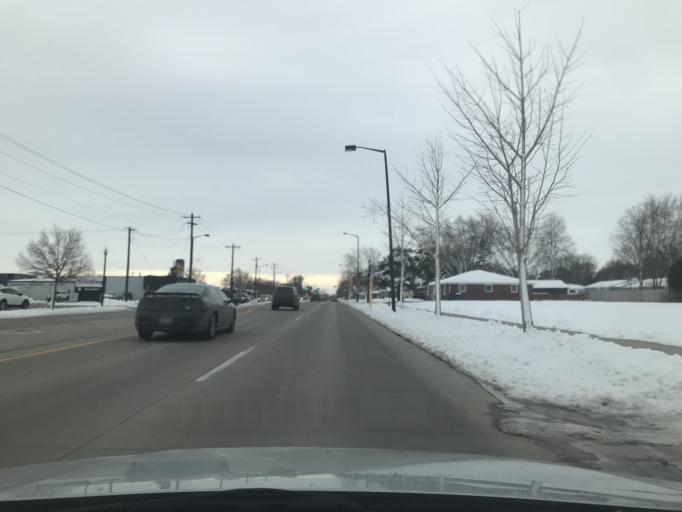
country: US
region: Wisconsin
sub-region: Brown County
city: Ashwaubenon
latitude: 44.4974
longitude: -88.0599
